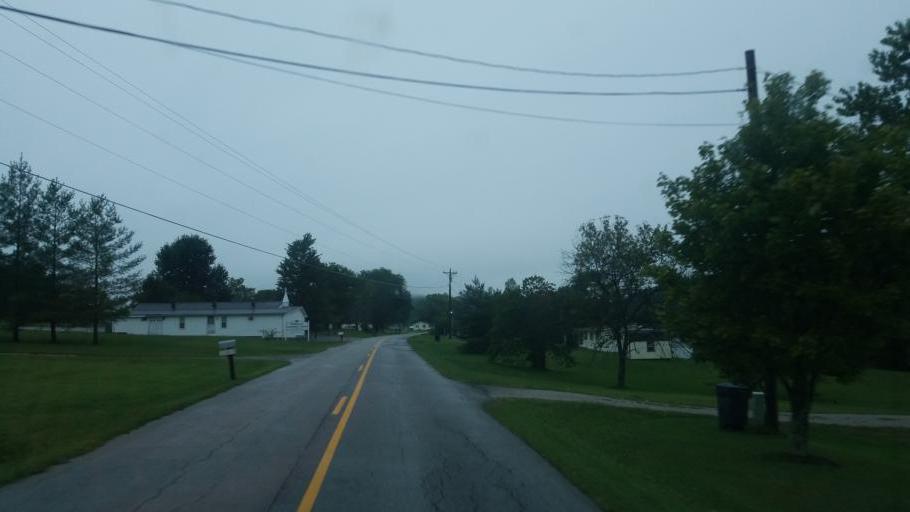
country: US
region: Kentucky
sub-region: Fleming County
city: Flemingsburg
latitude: 38.4032
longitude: -83.6266
